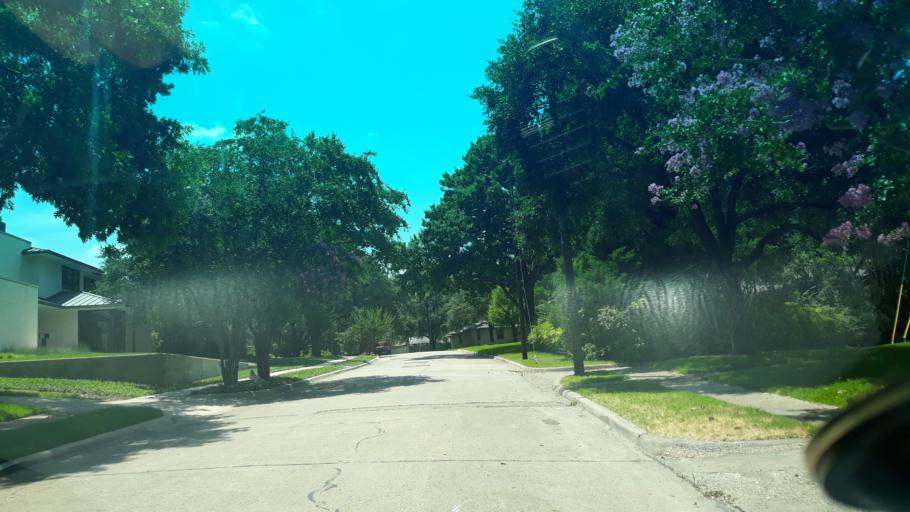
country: US
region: Texas
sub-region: Dallas County
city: Highland Park
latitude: 32.8310
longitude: -96.7366
